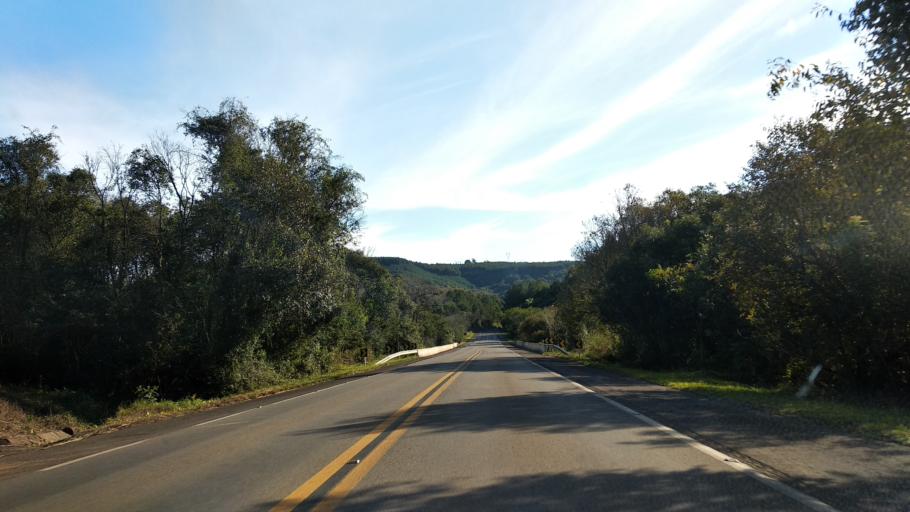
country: BR
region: Santa Catarina
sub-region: Celso Ramos
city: Celso Ramos
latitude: -27.5494
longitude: -51.4410
